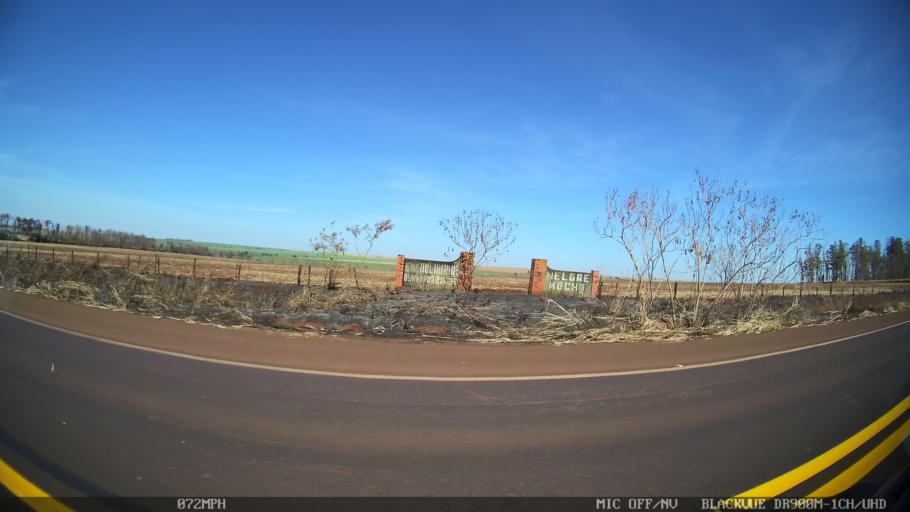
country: BR
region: Sao Paulo
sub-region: Barretos
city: Barretos
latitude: -20.4893
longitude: -48.5199
